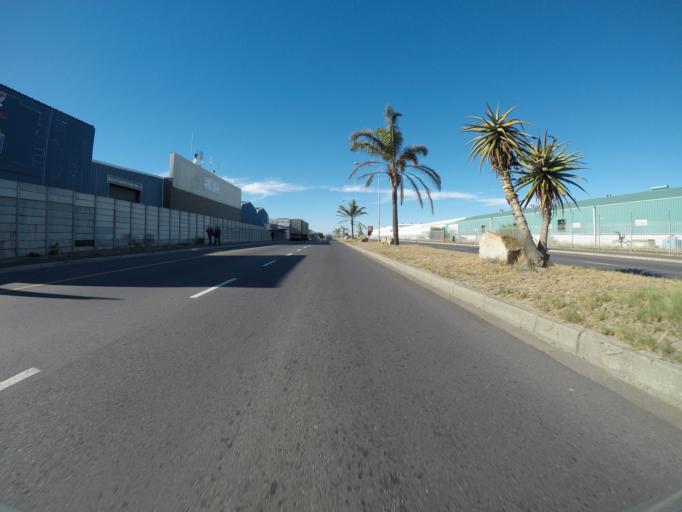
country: ZA
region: Western Cape
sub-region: City of Cape Town
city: Kraaifontein
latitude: -33.9021
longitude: 18.6691
